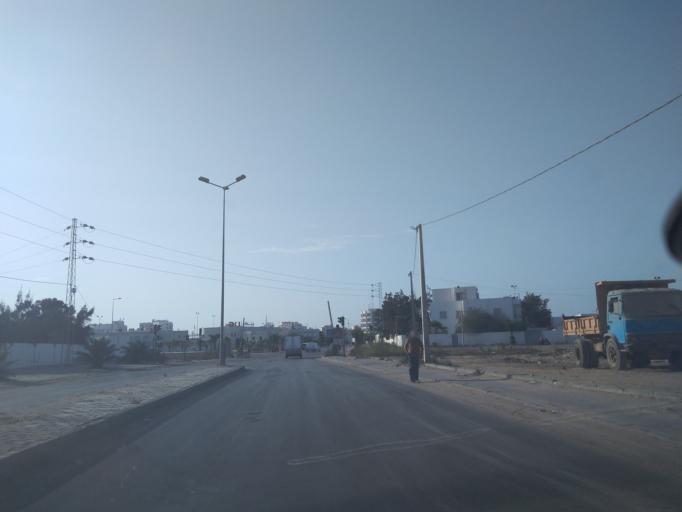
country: TN
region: Safaqis
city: Sfax
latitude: 34.7263
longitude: 10.7557
